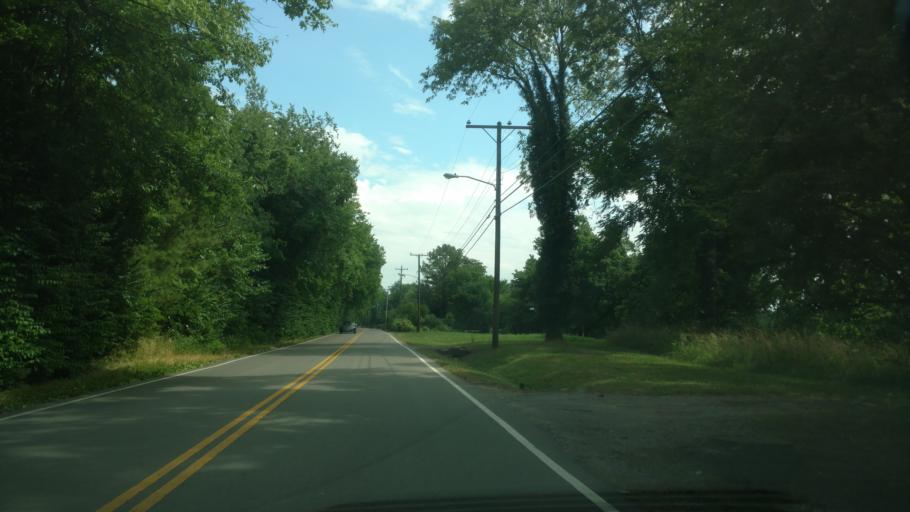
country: US
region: Tennessee
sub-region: Davidson County
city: Lakewood
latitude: 36.2229
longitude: -86.7064
